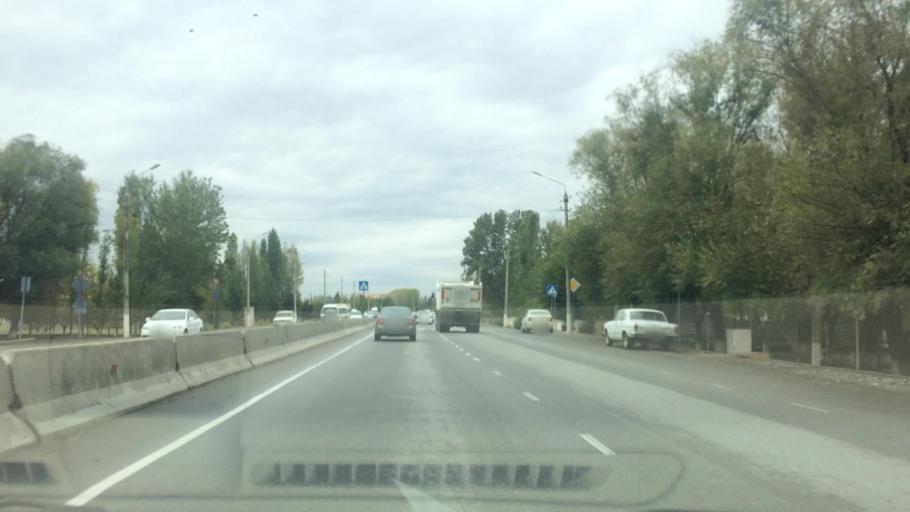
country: UZ
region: Jizzax
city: Jizzax
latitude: 39.9934
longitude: 67.5851
